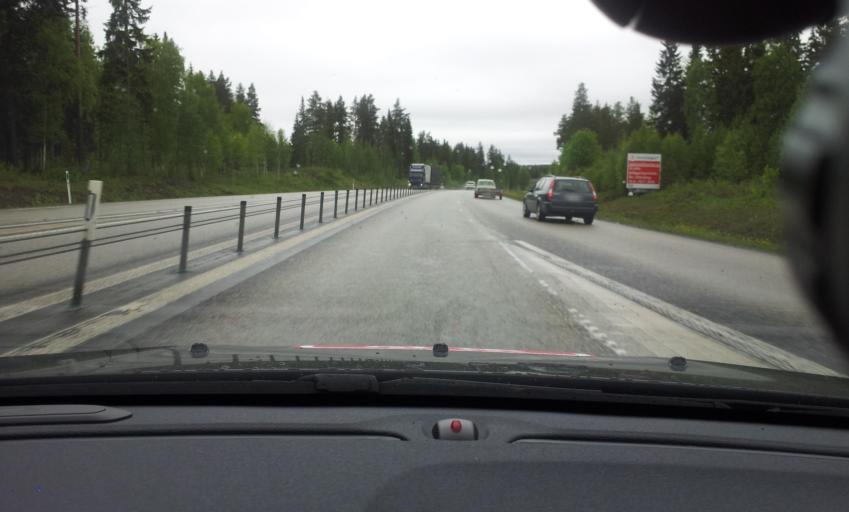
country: SE
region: Jaemtland
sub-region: OEstersunds Kommun
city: Ostersund
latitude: 63.1813
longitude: 14.6895
